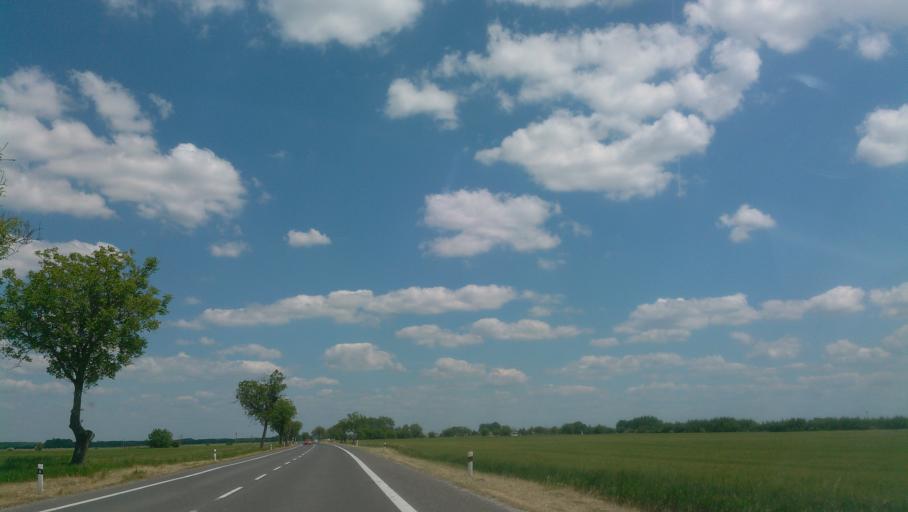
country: SK
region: Trnavsky
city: Dunajska Streda
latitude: 48.0003
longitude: 17.4638
